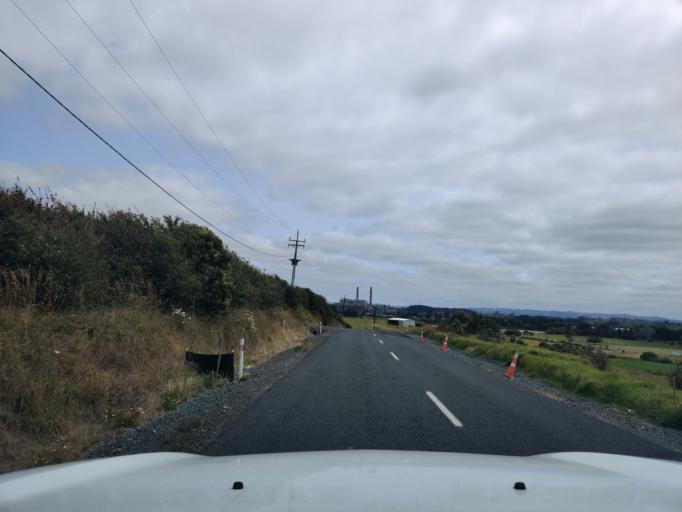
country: NZ
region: Waikato
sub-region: Waikato District
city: Te Kauwhata
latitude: -37.5243
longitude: 175.1738
